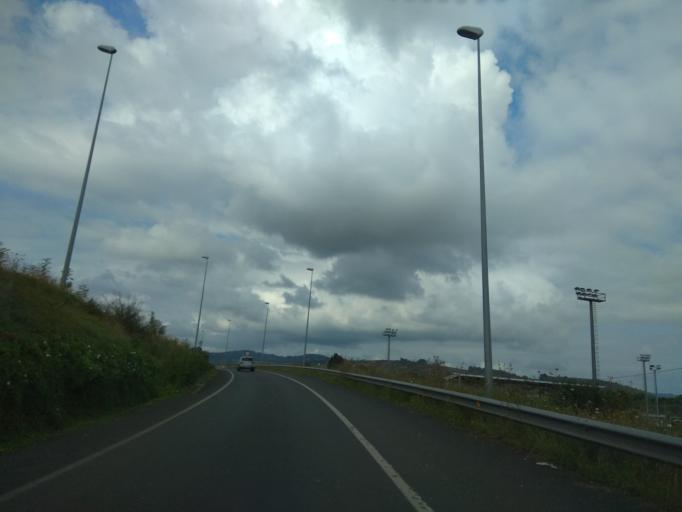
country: ES
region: Cantabria
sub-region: Provincia de Cantabria
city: Torrelavega
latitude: 43.3297
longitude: -4.0459
